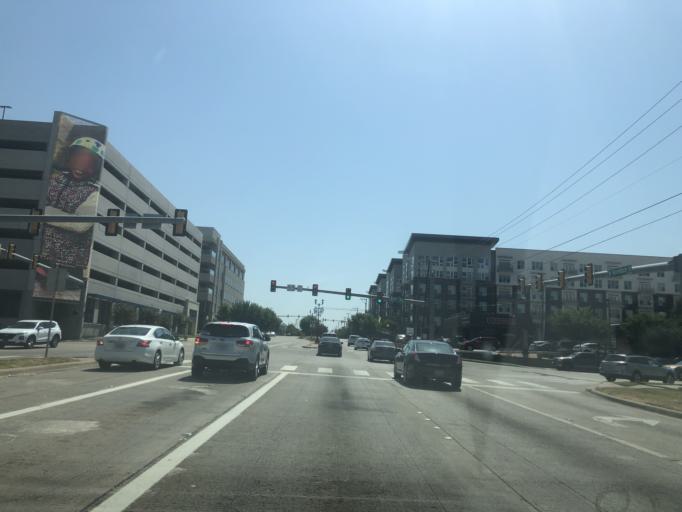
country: US
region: Texas
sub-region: Tarrant County
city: Fort Worth
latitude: 32.7331
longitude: -97.3443
